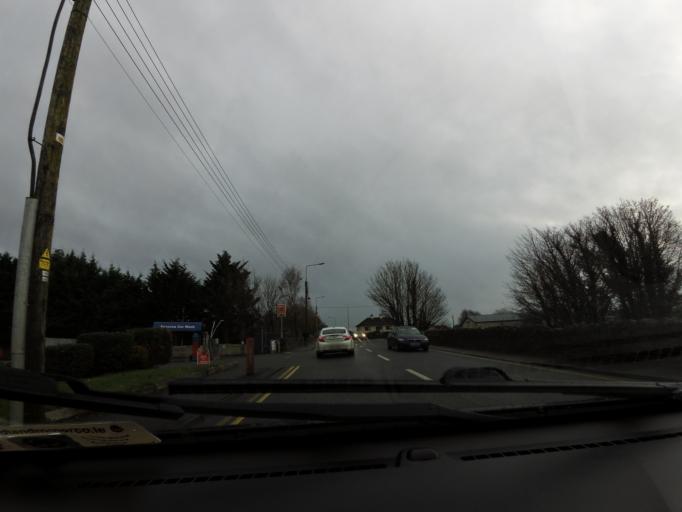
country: IE
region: Munster
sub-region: North Tipperary
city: Roscrea
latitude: 52.9581
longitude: -7.8013
